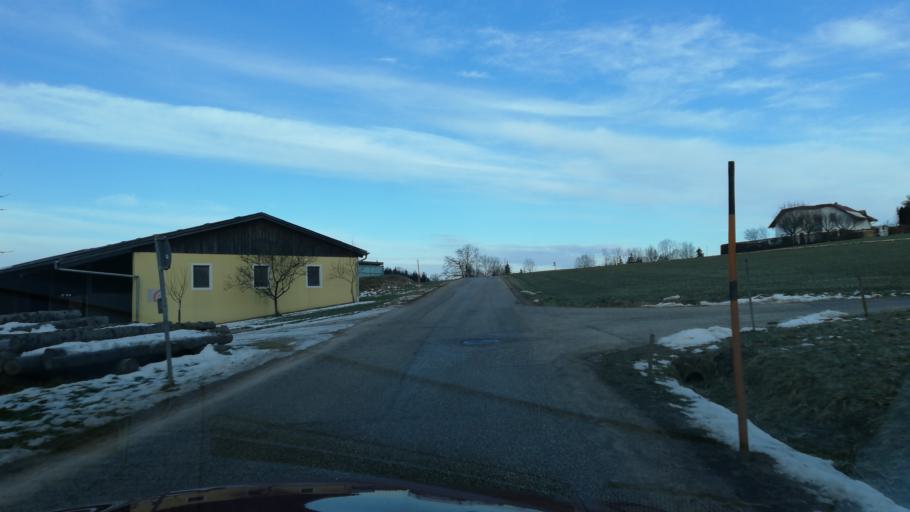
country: AT
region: Upper Austria
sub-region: Wels-Land
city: Buchkirchen
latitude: 48.2330
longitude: 13.9980
